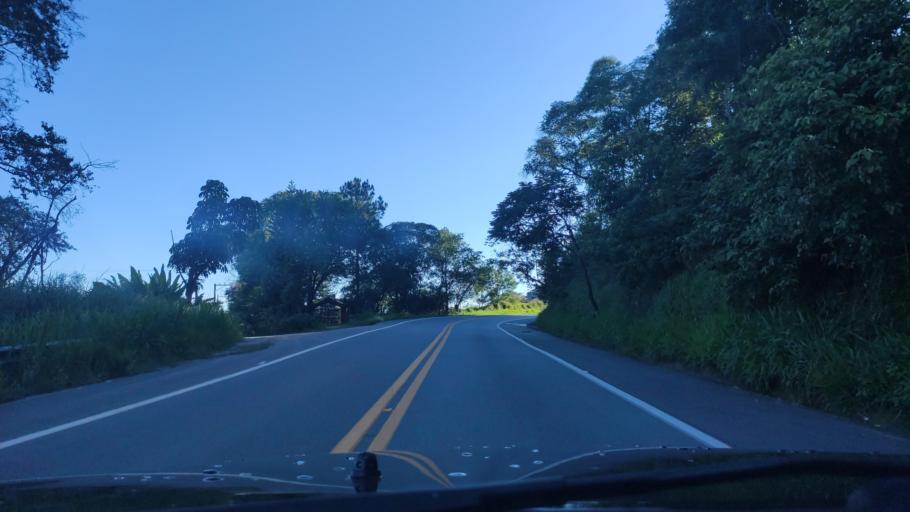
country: BR
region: Sao Paulo
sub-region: Socorro
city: Socorro
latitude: -22.5594
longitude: -46.5886
